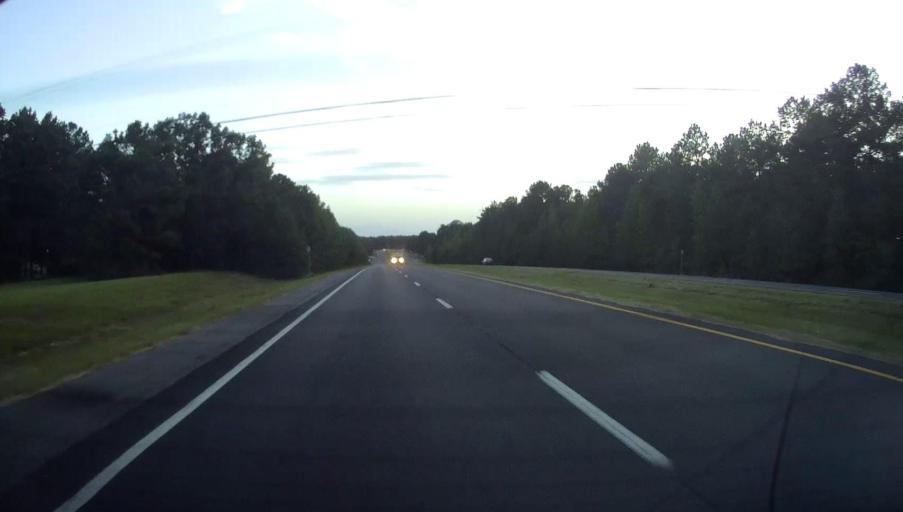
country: US
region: Georgia
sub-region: Muscogee County
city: Columbus
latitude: 32.5272
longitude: -84.8862
